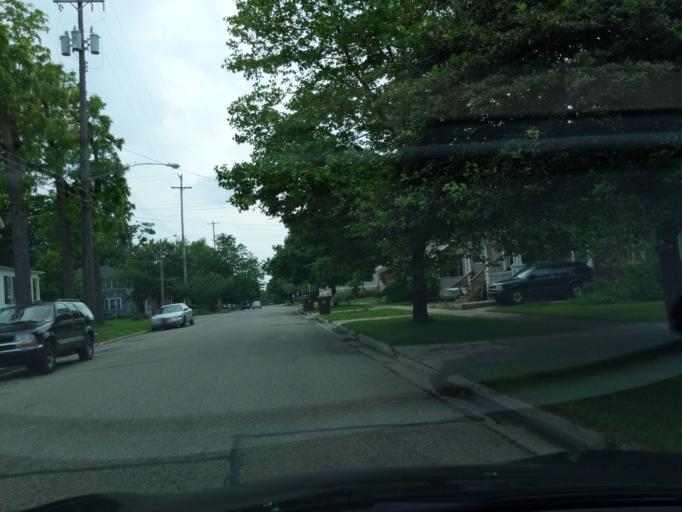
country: US
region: Michigan
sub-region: Ingham County
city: Lansing
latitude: 42.7448
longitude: -84.5530
